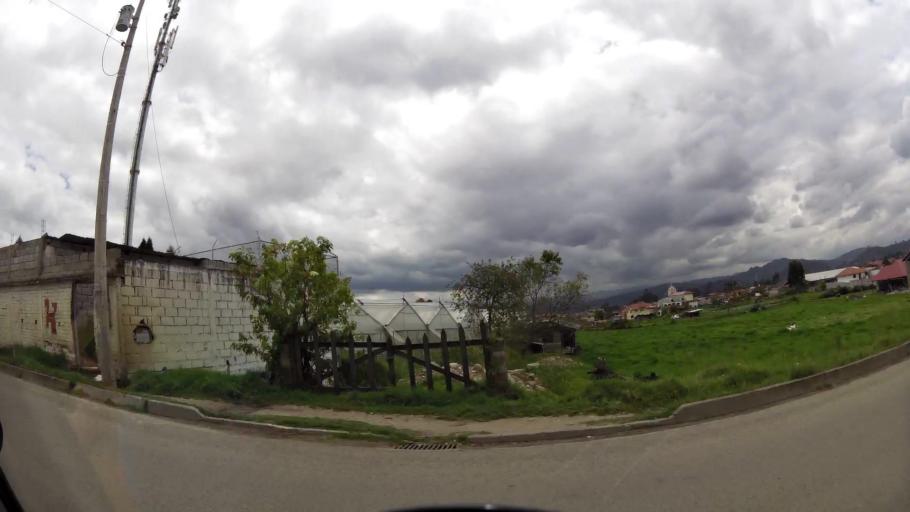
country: EC
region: Azuay
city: Cuenca
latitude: -2.8940
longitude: -79.0544
